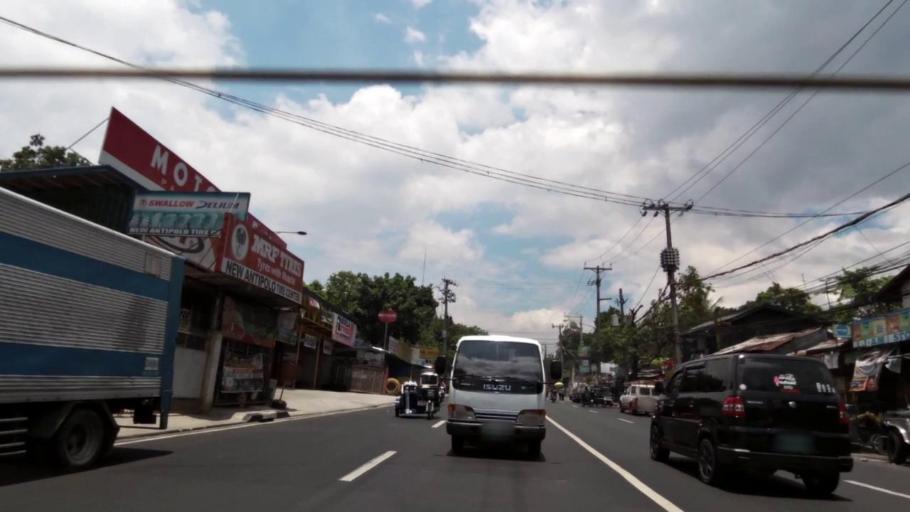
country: PH
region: Calabarzon
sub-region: Province of Rizal
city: Antipolo
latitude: 14.6032
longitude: 121.1753
